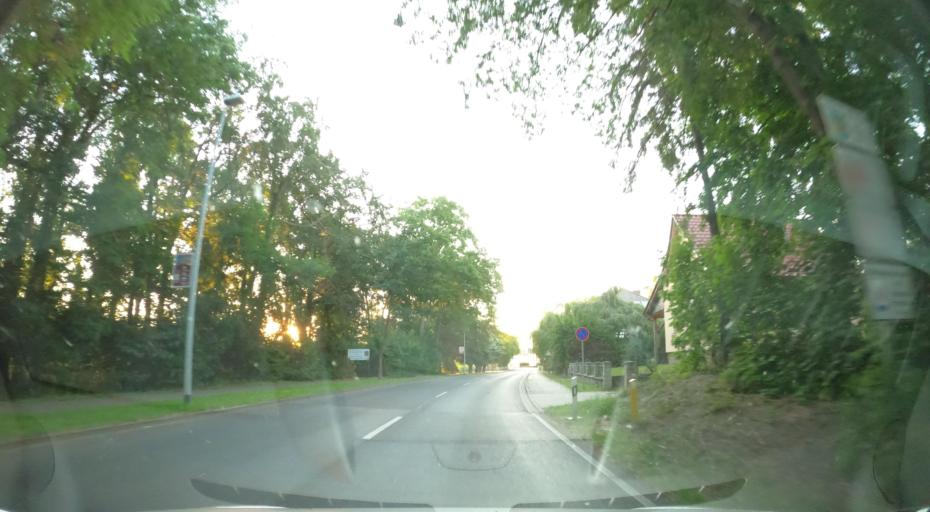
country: DE
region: Mecklenburg-Vorpommern
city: Strasburg
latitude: 53.5033
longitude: 13.7545
